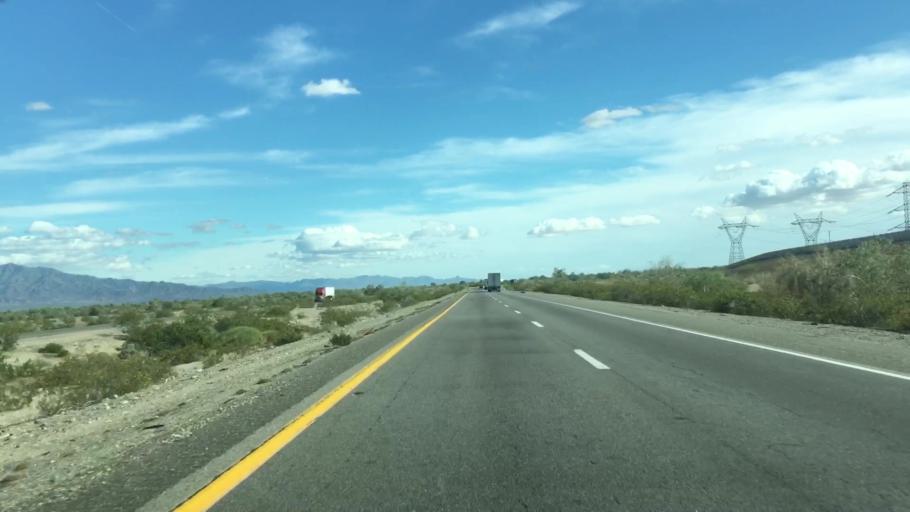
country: US
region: California
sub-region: Imperial County
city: Niland
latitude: 33.7020
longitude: -115.3135
